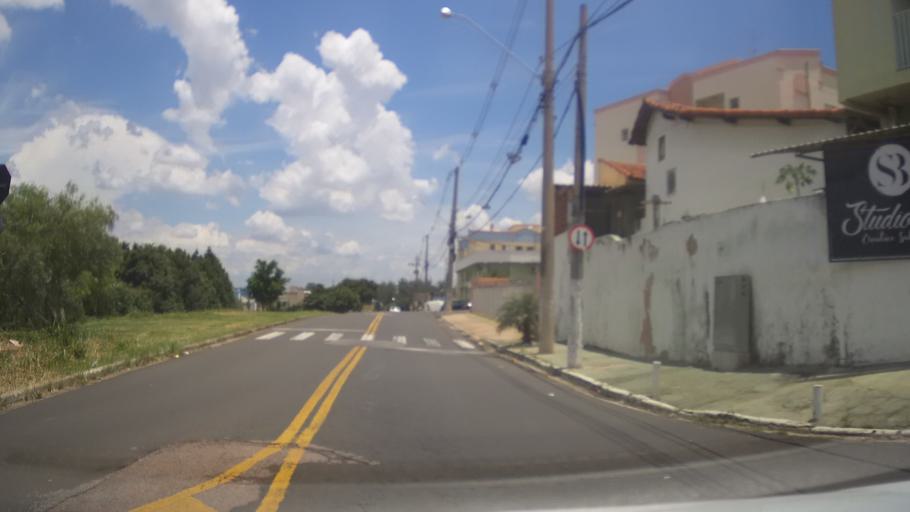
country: BR
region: Sao Paulo
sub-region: Valinhos
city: Valinhos
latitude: -22.9976
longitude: -46.9916
